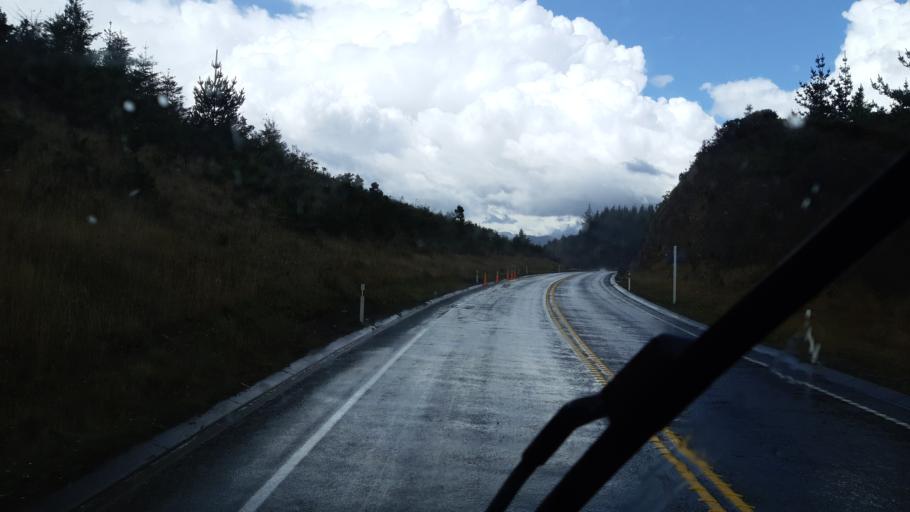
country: NZ
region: Tasman
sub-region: Tasman District
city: Wakefield
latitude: -41.4796
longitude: 172.9090
